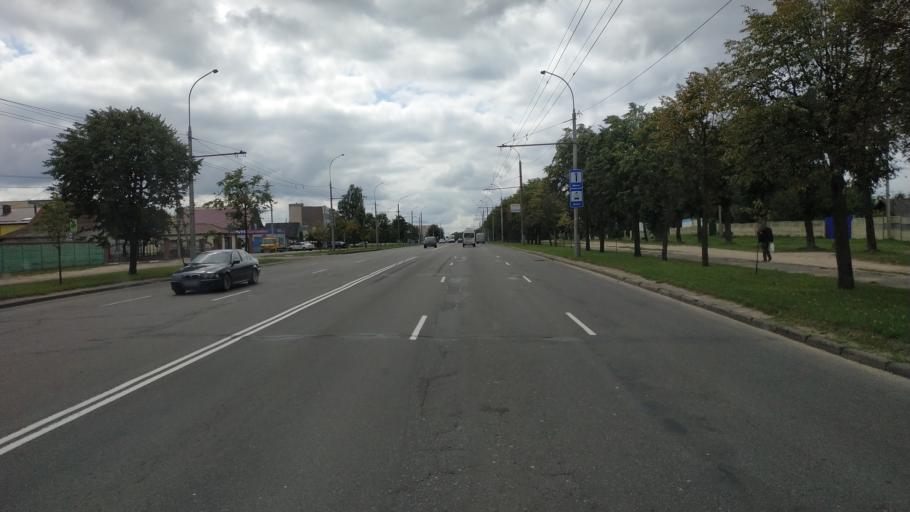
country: BY
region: Mogilev
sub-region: Mahilyowski Rayon
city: Veyno
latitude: 53.8686
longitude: 30.3655
